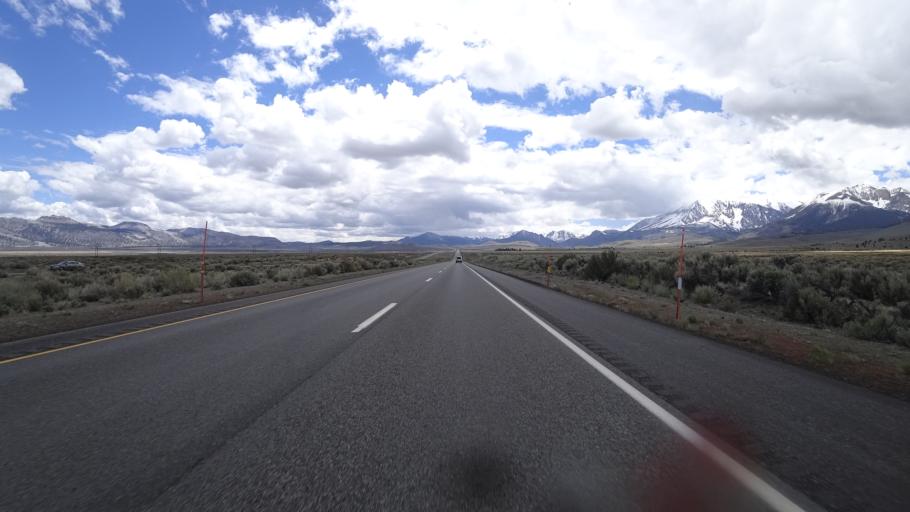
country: US
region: California
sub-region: Mono County
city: Mammoth Lakes
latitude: 37.9123
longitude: -119.0963
